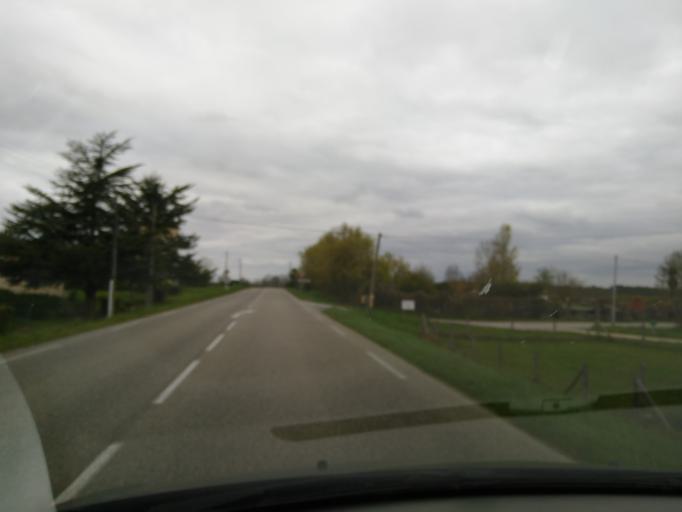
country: FR
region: Aquitaine
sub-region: Departement du Lot-et-Garonne
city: Cancon
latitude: 44.5007
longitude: 0.6662
